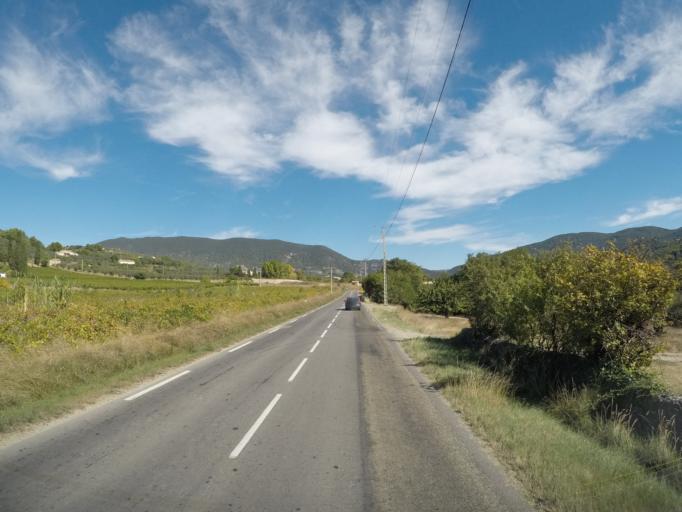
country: FR
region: Rhone-Alpes
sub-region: Departement de la Drome
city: Nyons
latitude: 44.3457
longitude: 5.1071
